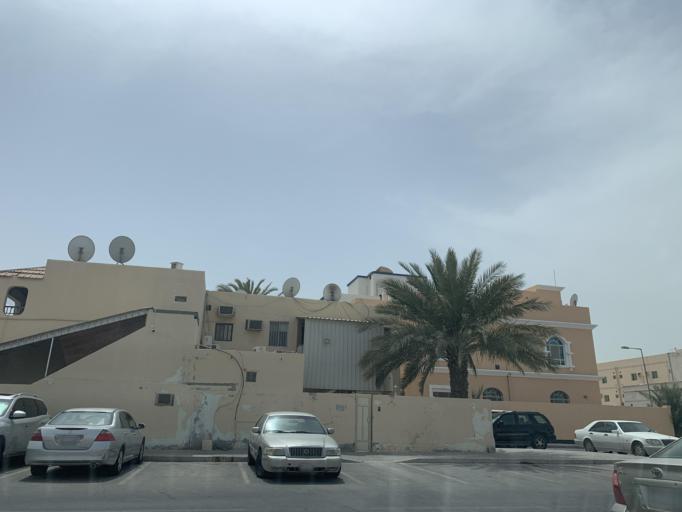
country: BH
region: Northern
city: Ar Rifa'
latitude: 26.1335
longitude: 50.5623
